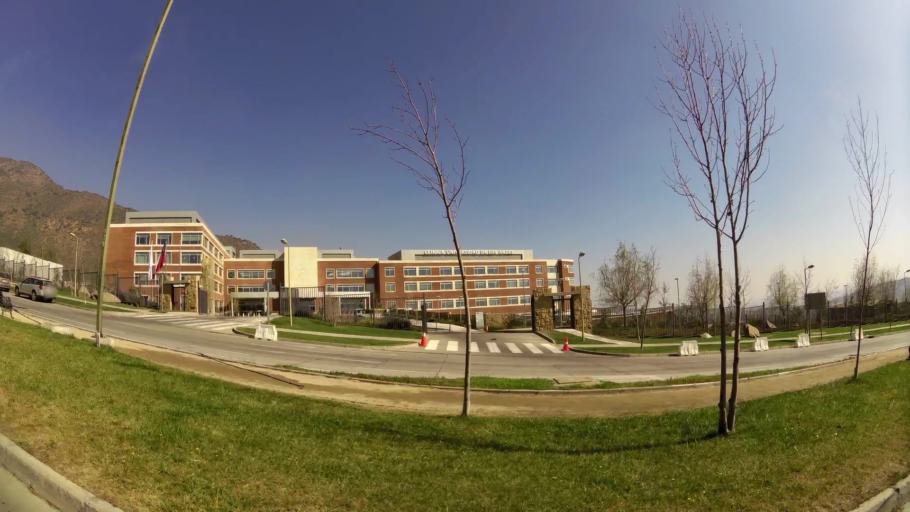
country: CL
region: Santiago Metropolitan
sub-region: Provincia de Santiago
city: Villa Presidente Frei, Nunoa, Santiago, Chile
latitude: -33.4048
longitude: -70.5034
